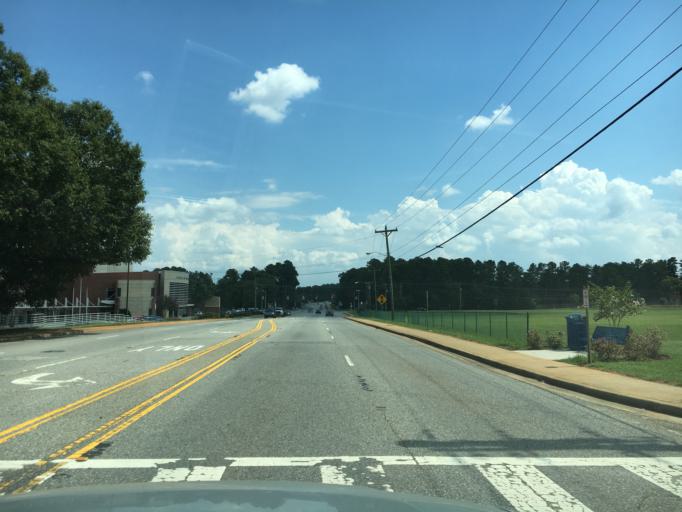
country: US
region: South Carolina
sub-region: Spartanburg County
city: Lyman
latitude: 34.9325
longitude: -82.1286
